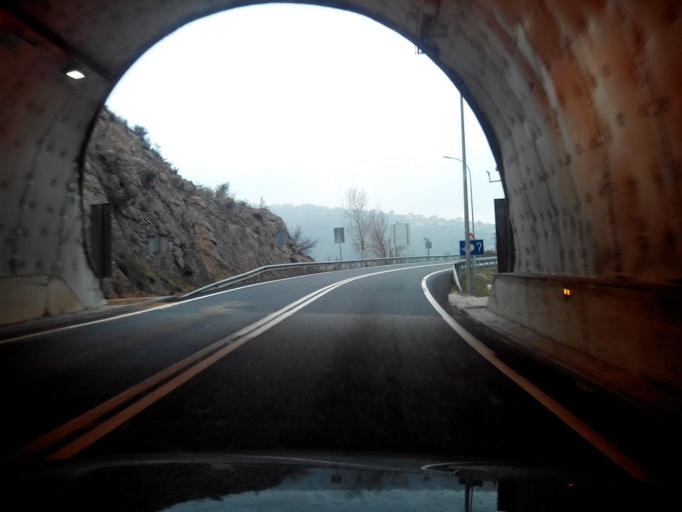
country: ES
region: Catalonia
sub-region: Provincia de Barcelona
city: Berga
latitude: 42.1141
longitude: 1.8582
